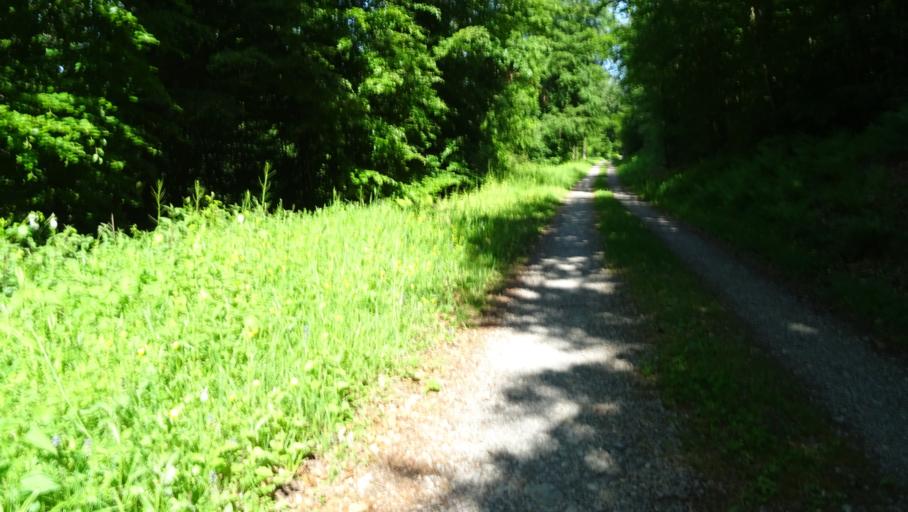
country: DE
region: Baden-Wuerttemberg
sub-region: Karlsruhe Region
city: Binau
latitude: 49.3803
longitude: 9.0509
